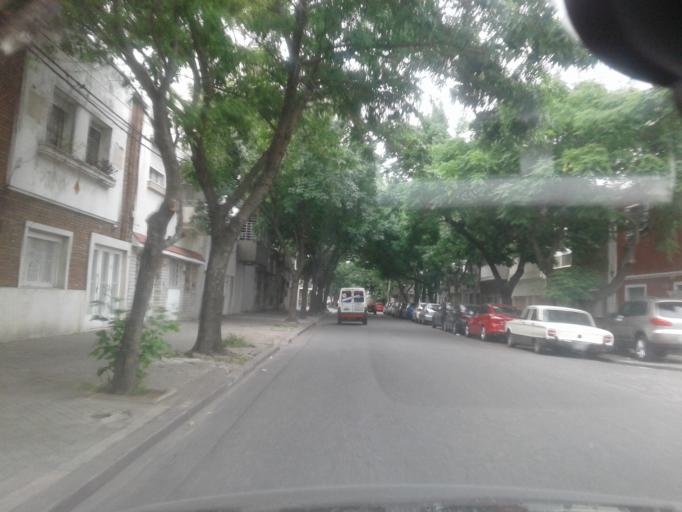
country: AR
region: Santa Fe
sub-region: Departamento de Rosario
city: Rosario
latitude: -32.9418
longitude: -60.6756
